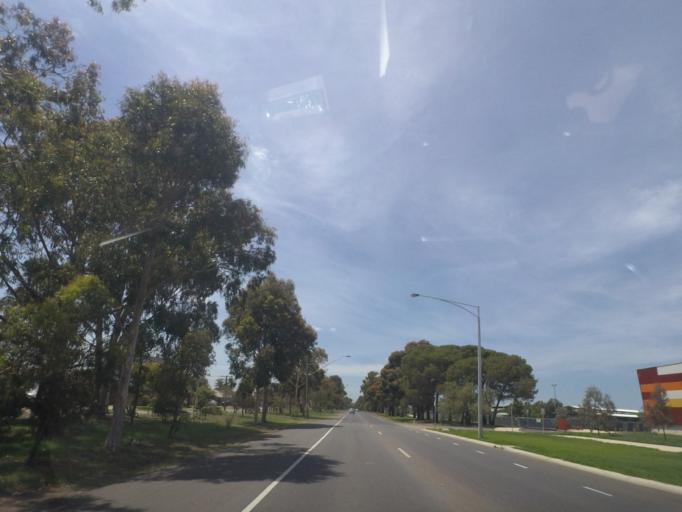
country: AU
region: Victoria
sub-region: Wyndham
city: Werribee
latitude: -37.8981
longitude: 144.6415
